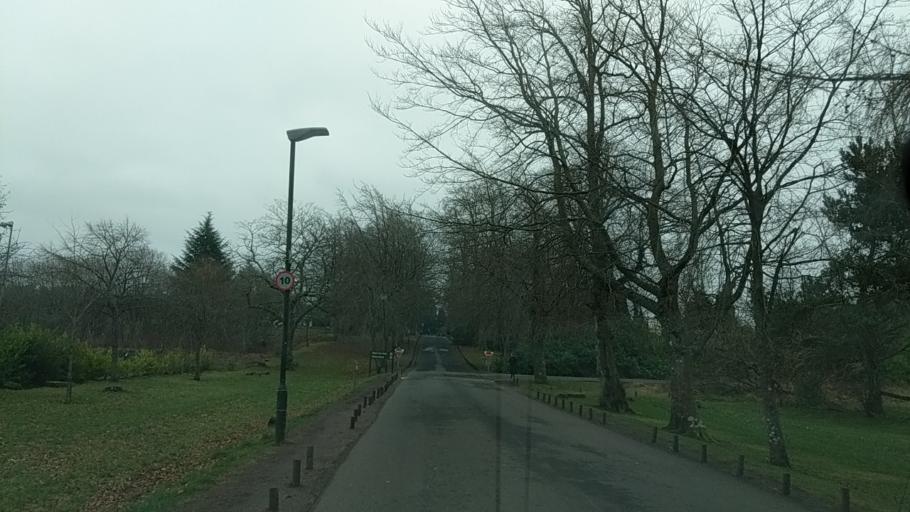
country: GB
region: Scotland
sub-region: South Lanarkshire
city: East Kilbride
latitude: 55.7500
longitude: -4.1485
